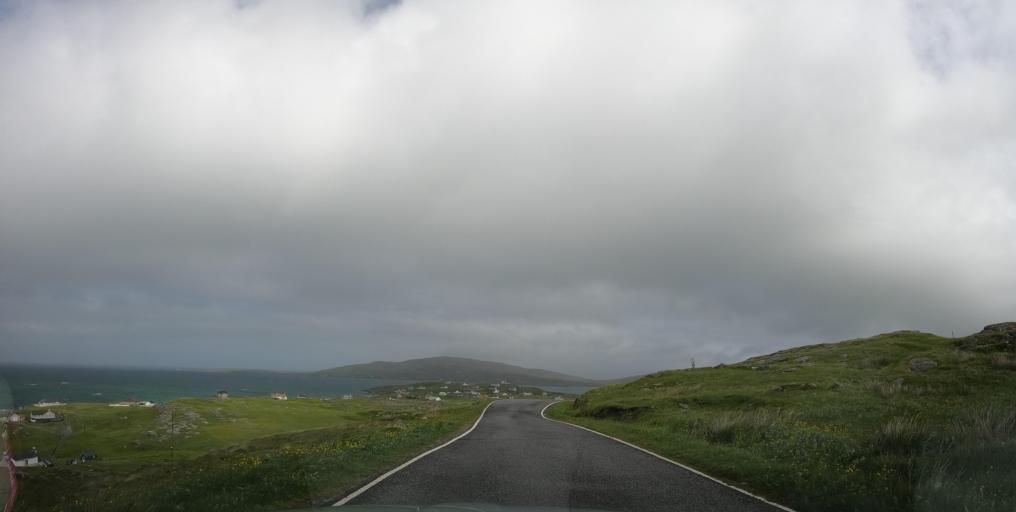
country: GB
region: Scotland
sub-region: Eilean Siar
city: Isle of South Uist
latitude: 57.0779
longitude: -7.3026
